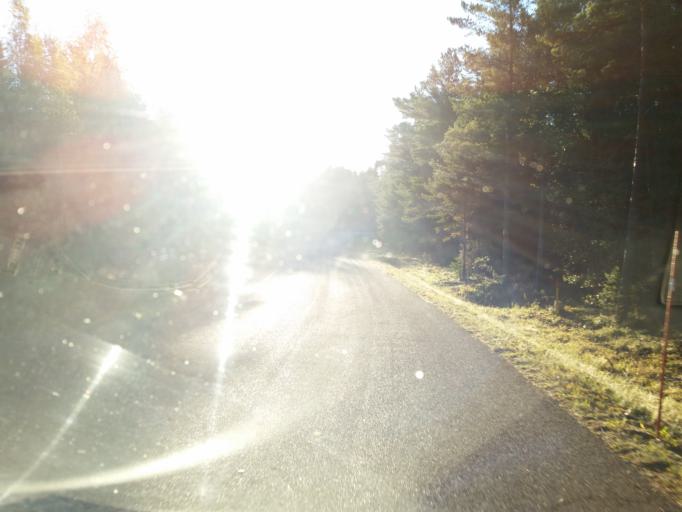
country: AX
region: Alands skaergard
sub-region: Vardoe
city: Vardoe
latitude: 60.2905
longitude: 20.3876
